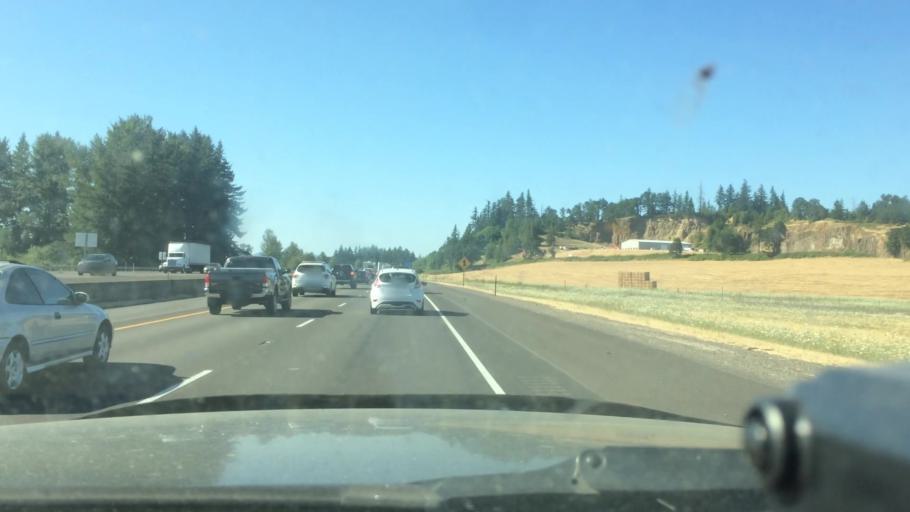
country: US
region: Oregon
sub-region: Linn County
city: Millersburg
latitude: 44.7057
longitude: -123.0526
